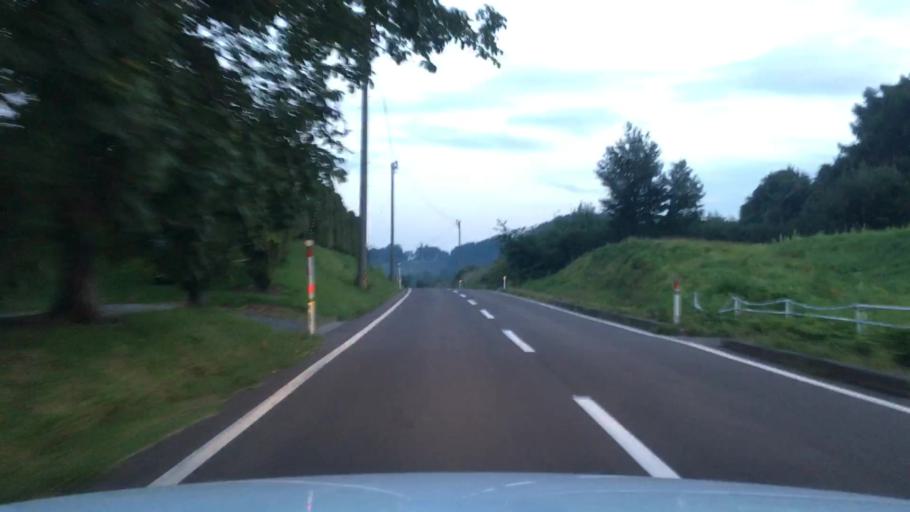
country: JP
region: Aomori
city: Hirosaki
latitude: 40.6738
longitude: 140.3846
